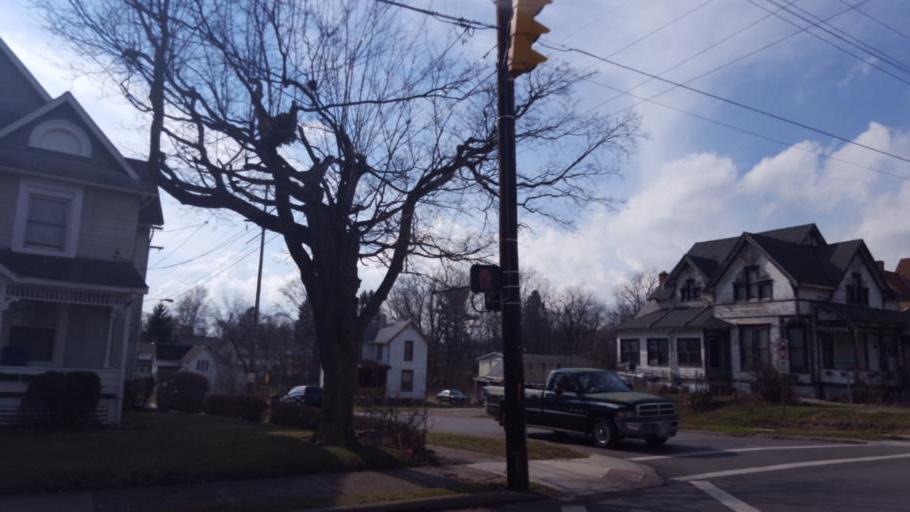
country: US
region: Ohio
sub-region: Richland County
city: Mansfield
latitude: 40.7714
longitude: -82.5277
